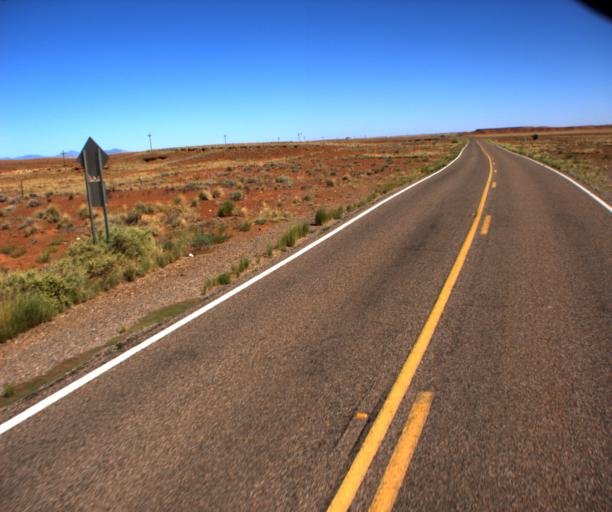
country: US
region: Arizona
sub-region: Coconino County
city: LeChee
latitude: 35.1910
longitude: -110.9386
